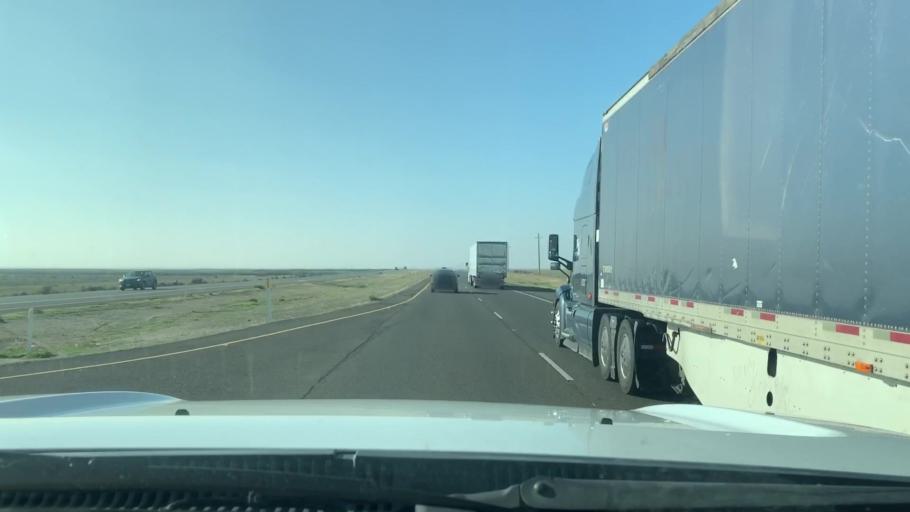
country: US
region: California
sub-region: Kern County
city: Lost Hills
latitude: 35.6159
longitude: -119.7758
